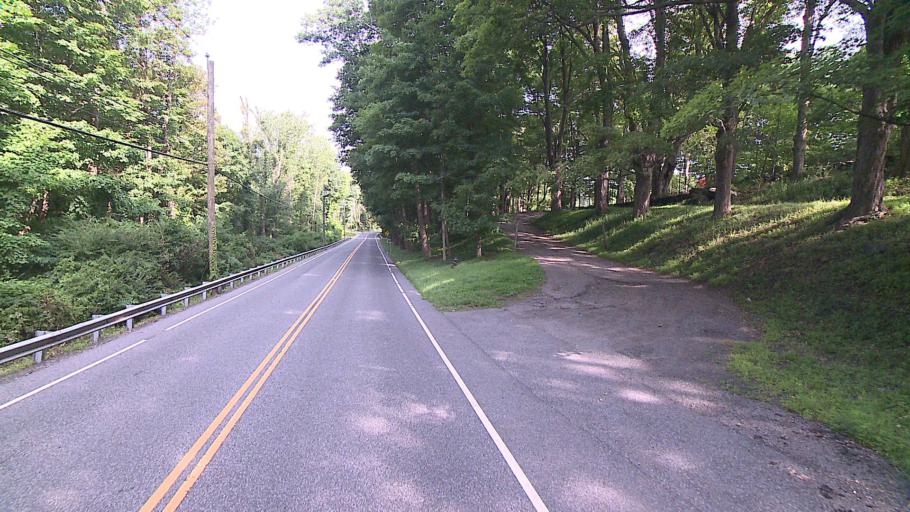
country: US
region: Connecticut
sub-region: Fairfield County
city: Sherman
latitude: 41.5627
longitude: -73.5054
